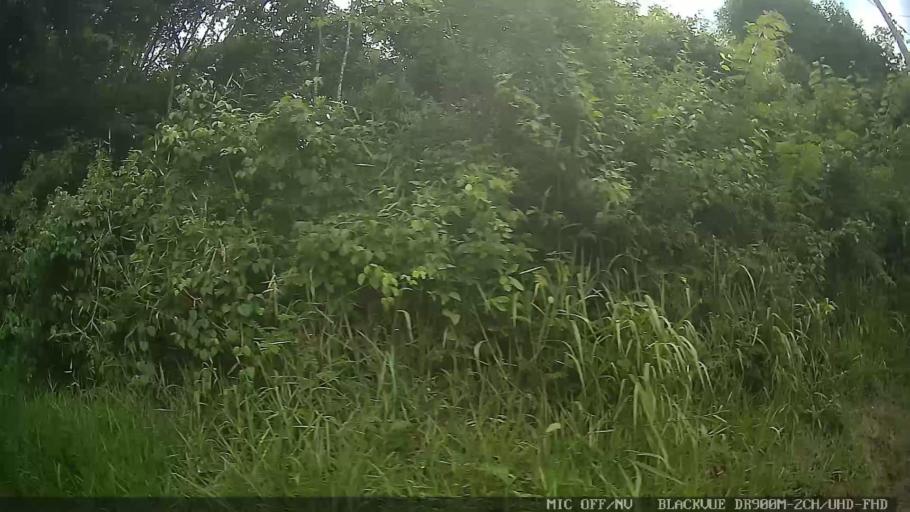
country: BR
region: Minas Gerais
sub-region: Extrema
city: Extrema
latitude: -22.8415
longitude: -46.2892
